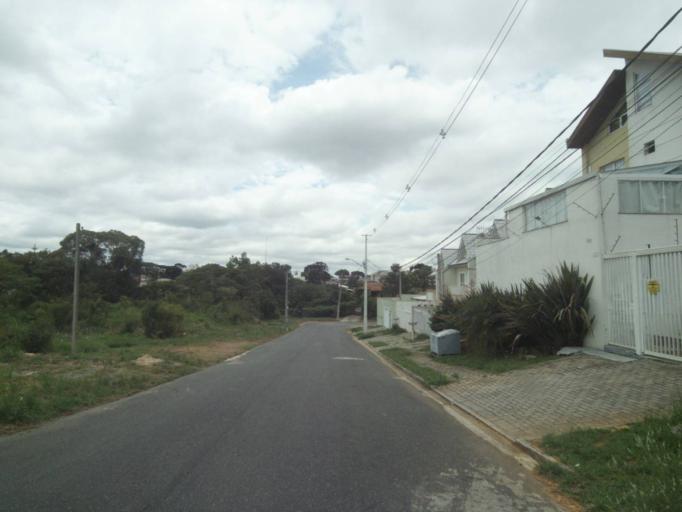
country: BR
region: Parana
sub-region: Curitiba
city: Curitiba
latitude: -25.3919
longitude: -49.2867
